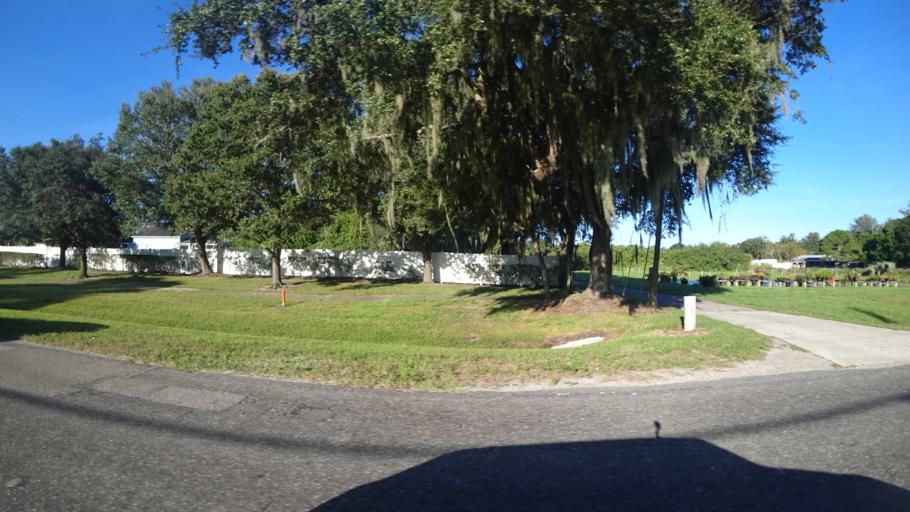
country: US
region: Florida
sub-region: Manatee County
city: Memphis
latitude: 27.5790
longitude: -82.5274
